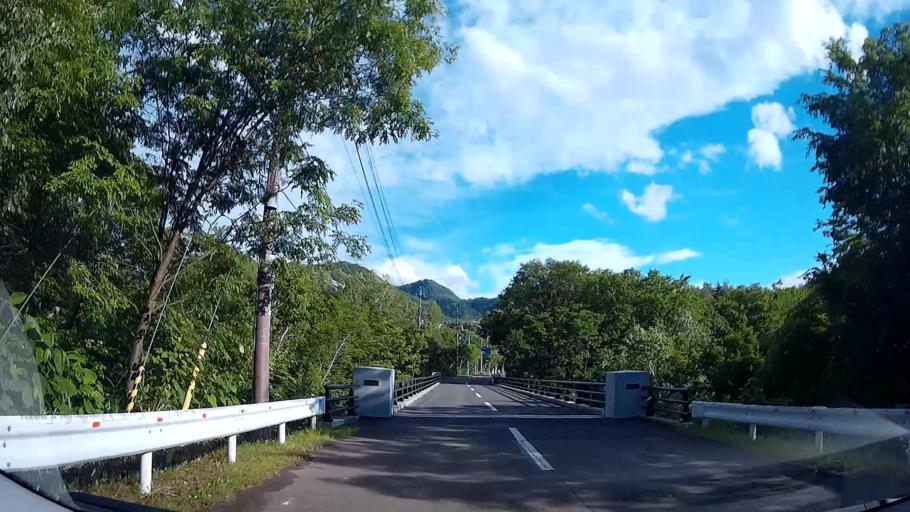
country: JP
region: Hokkaido
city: Sapporo
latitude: 42.9743
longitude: 141.1659
